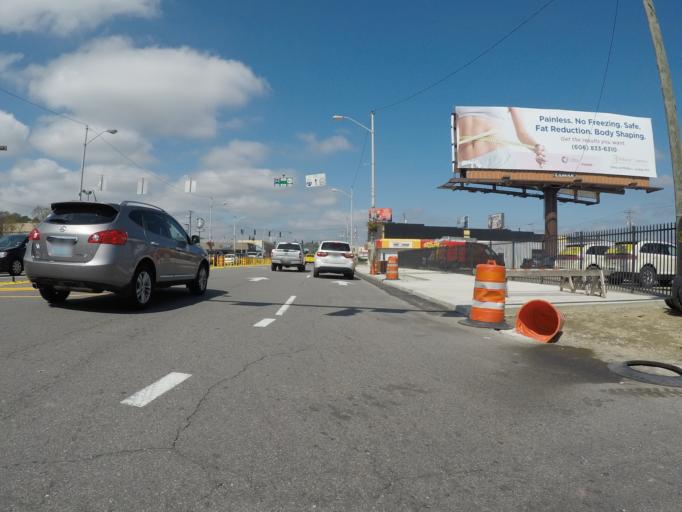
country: US
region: Kentucky
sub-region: Boyd County
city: Ashland
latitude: 38.4805
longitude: -82.6431
